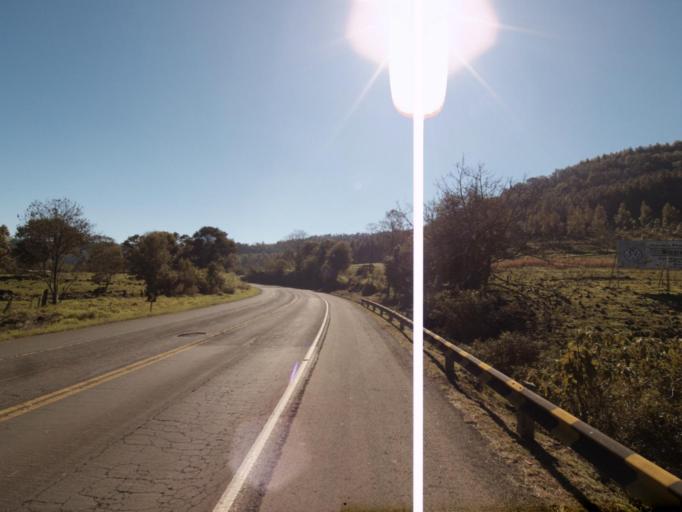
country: BR
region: Rio Grande do Sul
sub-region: Frederico Westphalen
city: Frederico Westphalen
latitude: -26.9767
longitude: -53.2140
